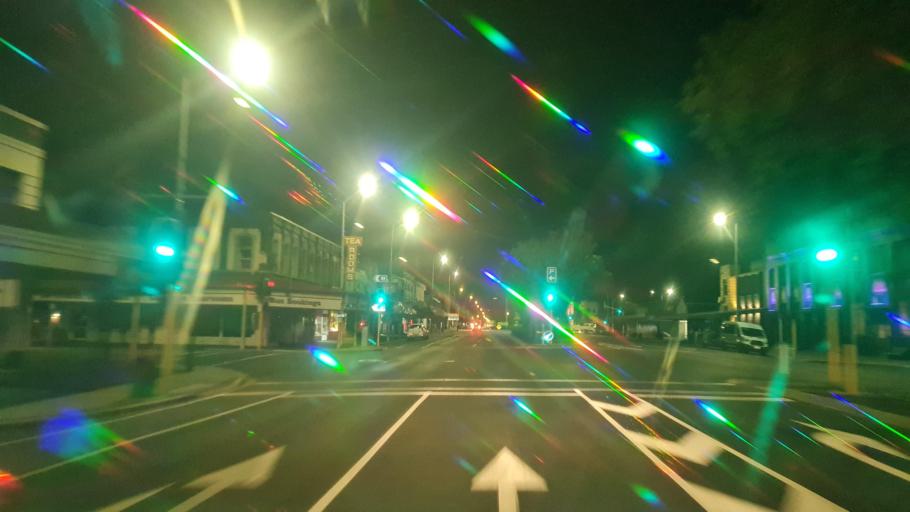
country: NZ
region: Otago
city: Oamaru
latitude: -45.0963
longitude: 170.9718
